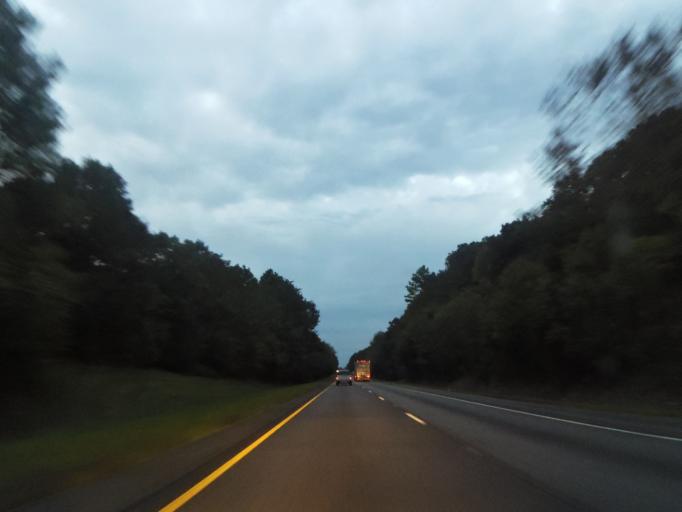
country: US
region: Alabama
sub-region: Etowah County
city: Whitesboro
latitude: 34.1638
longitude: -85.9744
